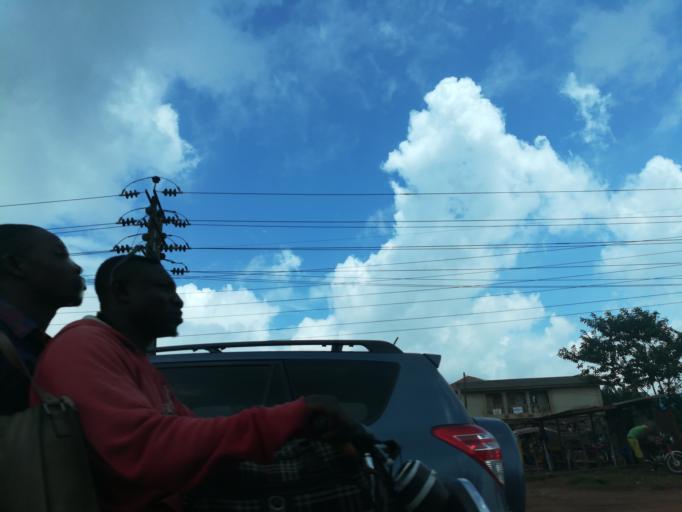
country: NG
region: Lagos
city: Ikorodu
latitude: 6.6600
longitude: 3.5195
